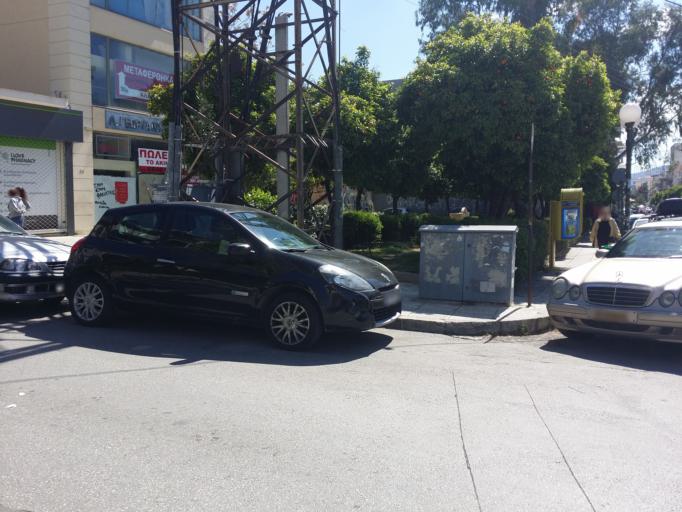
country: GR
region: Attica
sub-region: Nomarchia Athinas
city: Nea Ionia
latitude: 38.0455
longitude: 23.7536
